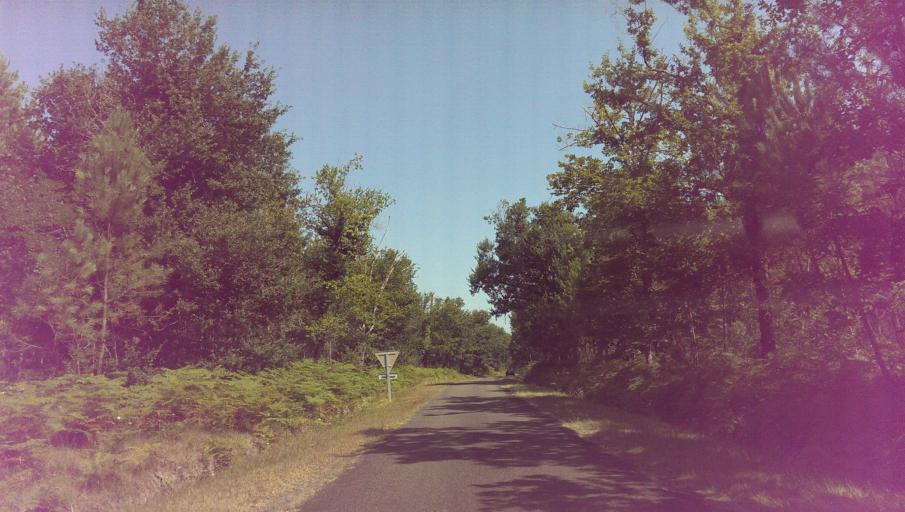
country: FR
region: Aquitaine
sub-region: Departement des Landes
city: Sarbazan
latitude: 44.0100
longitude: -0.1926
